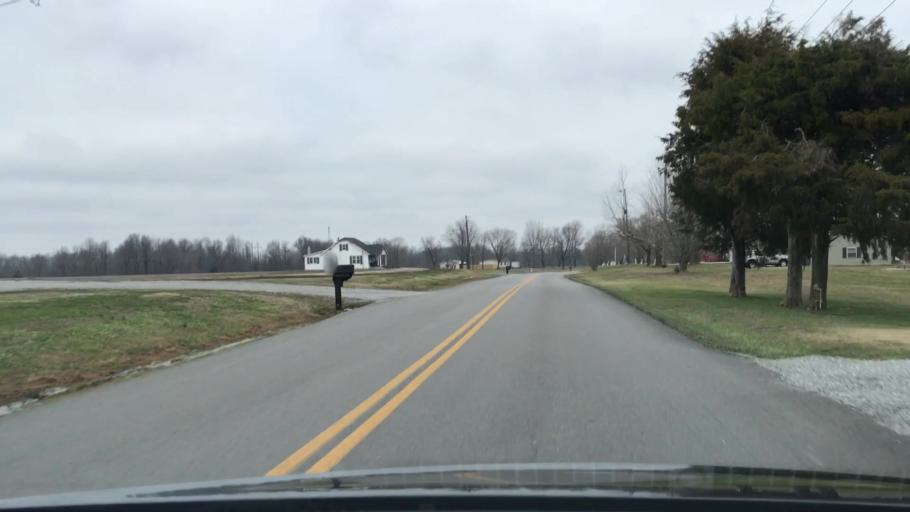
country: US
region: Kentucky
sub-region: Muhlenberg County
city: Morehead
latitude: 37.3353
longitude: -87.2201
